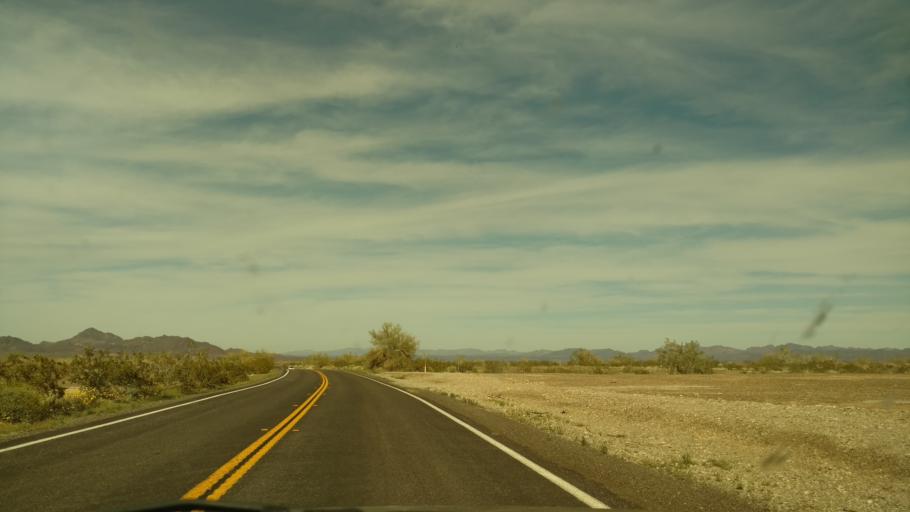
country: US
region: California
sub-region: Riverside County
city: Mesa Verde
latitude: 33.2373
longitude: -114.8362
